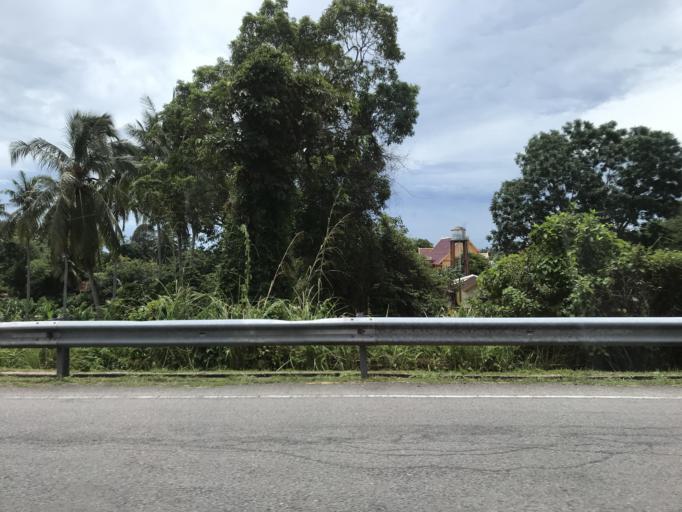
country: MY
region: Kelantan
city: Tumpat
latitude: 6.1774
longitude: 102.1870
